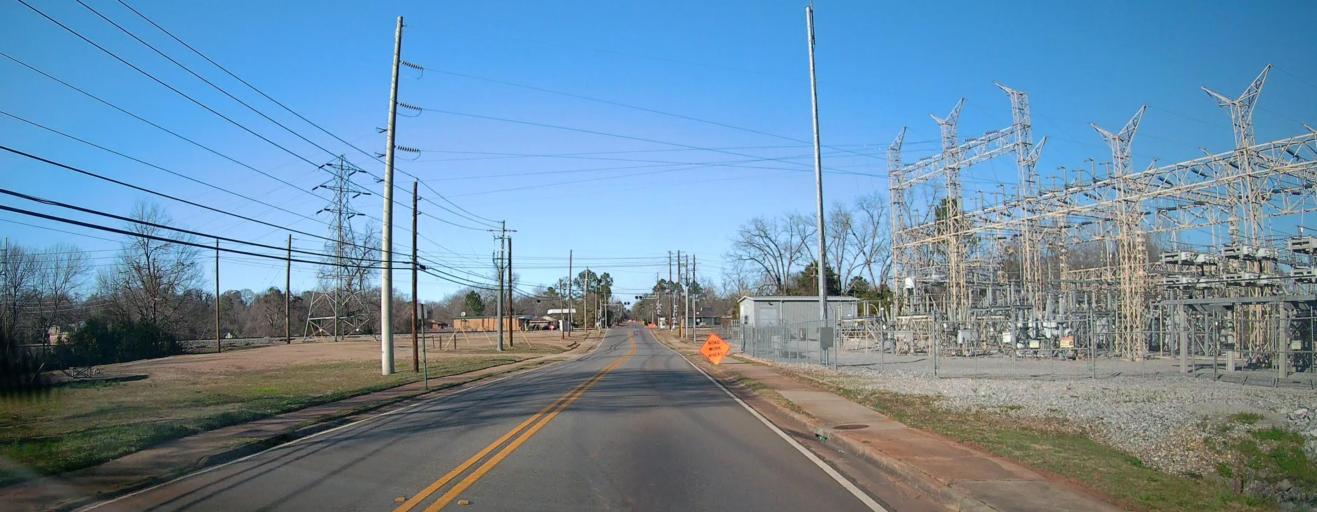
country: US
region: Georgia
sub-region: Sumter County
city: Americus
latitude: 32.0794
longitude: -84.2322
